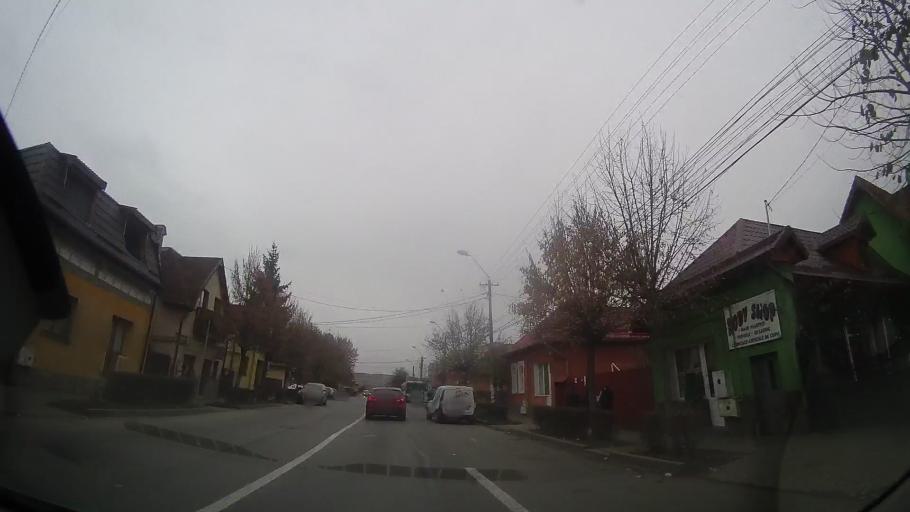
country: RO
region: Mures
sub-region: Comuna Santana de Mures
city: Santana de Mures
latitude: 46.5724
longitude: 24.5504
